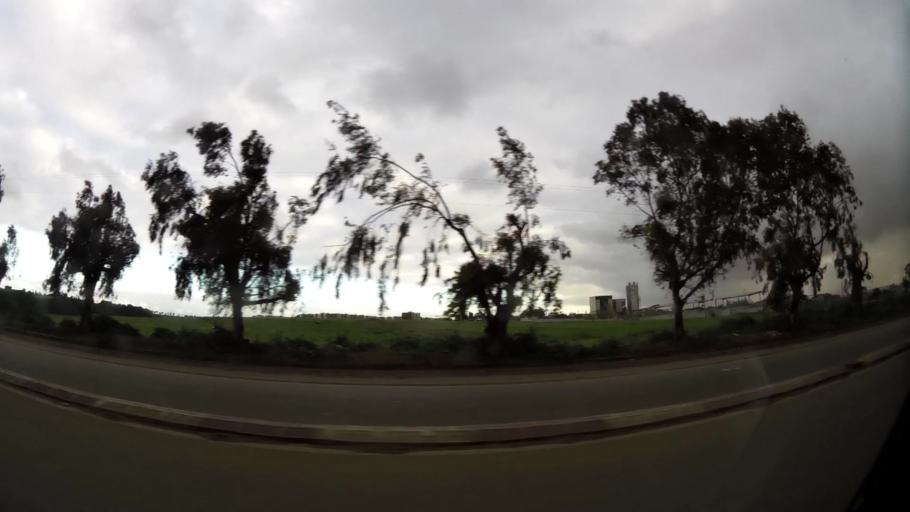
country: MA
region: Grand Casablanca
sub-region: Mediouna
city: Tit Mellil
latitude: 33.5668
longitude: -7.5067
